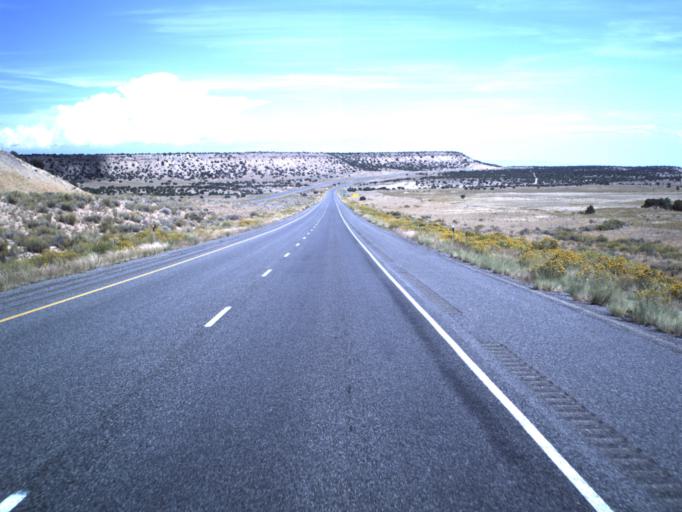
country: US
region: Utah
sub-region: Emery County
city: Castle Dale
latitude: 38.8995
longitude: -110.5717
